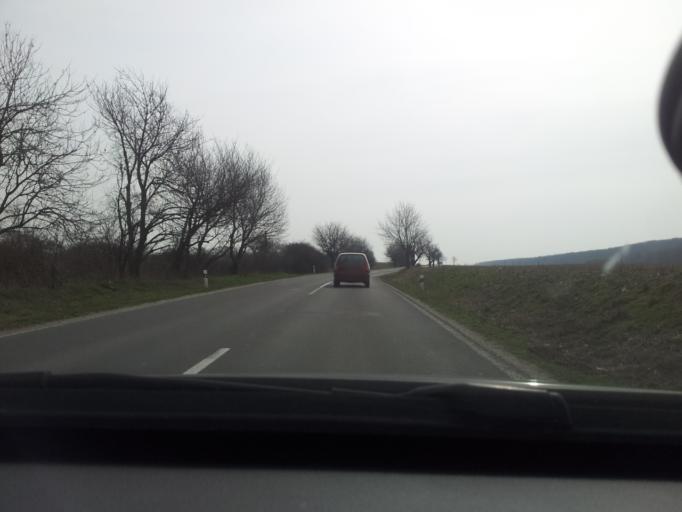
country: SK
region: Trnavsky
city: Hlohovec
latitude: 48.4097
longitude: 17.8389
